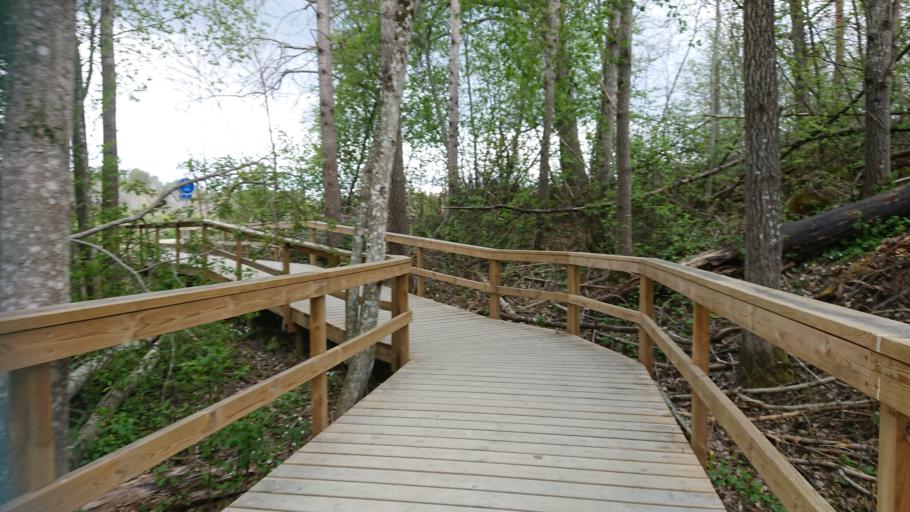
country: SE
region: Uppsala
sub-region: Uppsala Kommun
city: Uppsala
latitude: 59.7970
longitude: 17.6102
